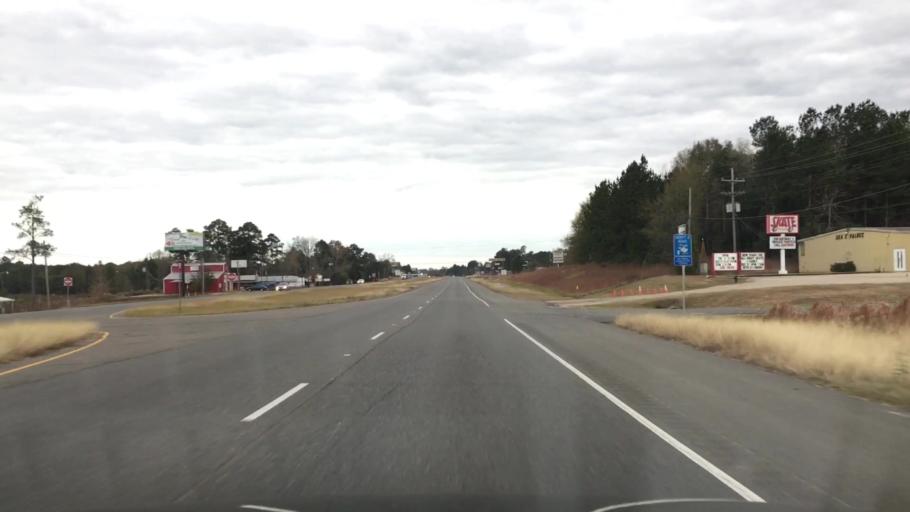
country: US
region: Louisiana
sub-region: Vernon Parish
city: New Llano
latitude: 31.0841
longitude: -93.2720
